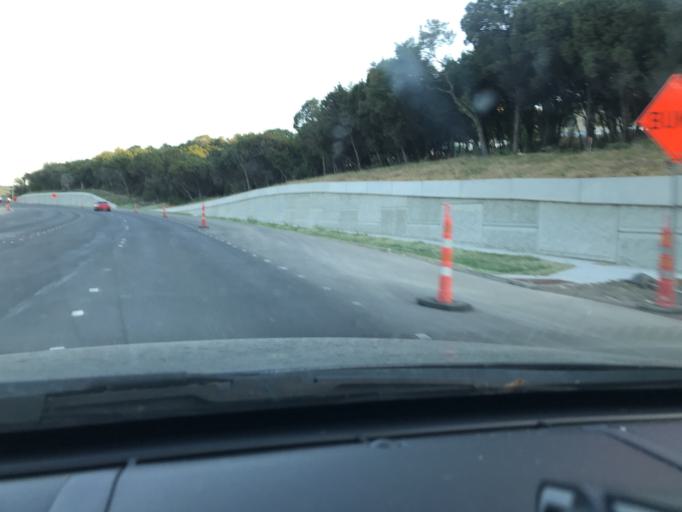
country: US
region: Texas
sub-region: Travis County
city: West Lake Hills
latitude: 30.2863
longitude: -97.8128
